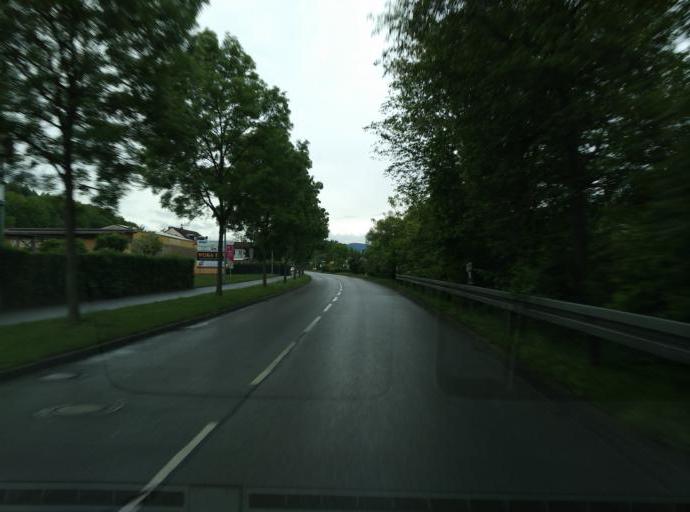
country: DE
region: Baden-Wuerttemberg
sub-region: Tuebingen Region
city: Wannweil
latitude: 48.5228
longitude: 9.1449
